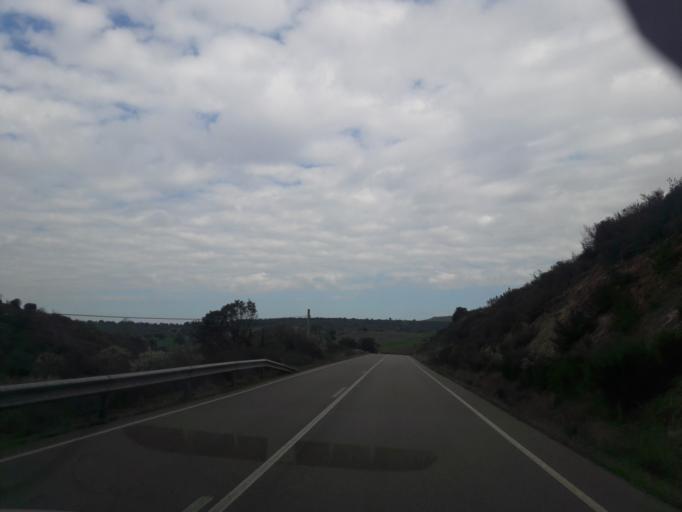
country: ES
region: Castille and Leon
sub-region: Provincia de Salamanca
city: Serradilla del Arroyo
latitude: 40.5175
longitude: -6.3644
